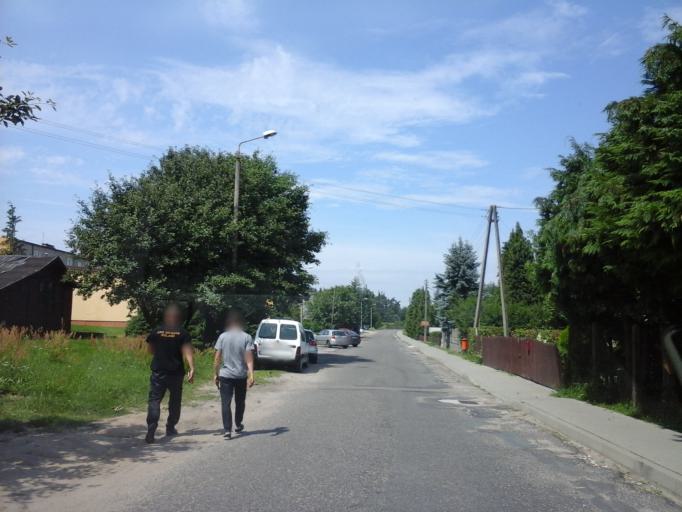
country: PL
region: West Pomeranian Voivodeship
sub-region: Powiat choszczenski
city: Bierzwnik
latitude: 53.0329
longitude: 15.6600
